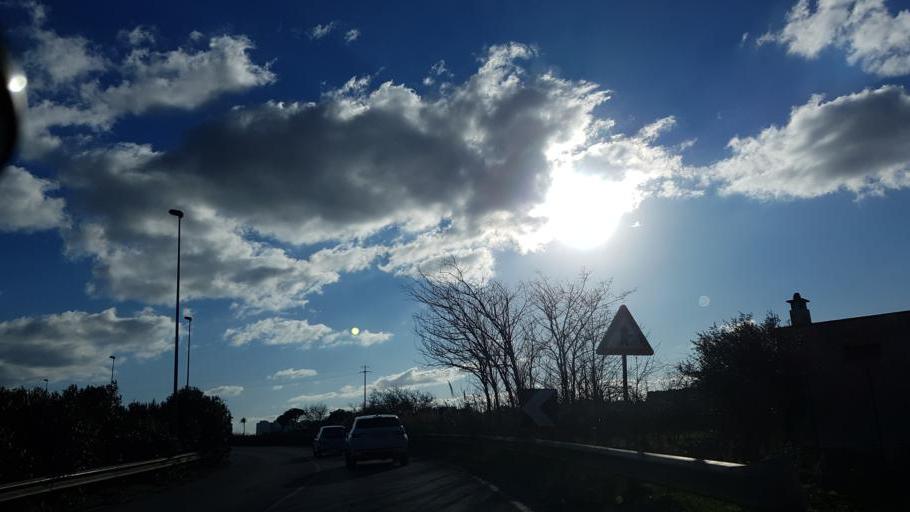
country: IT
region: Apulia
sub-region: Provincia di Brindisi
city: Brindisi
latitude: 40.6345
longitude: 17.9181
